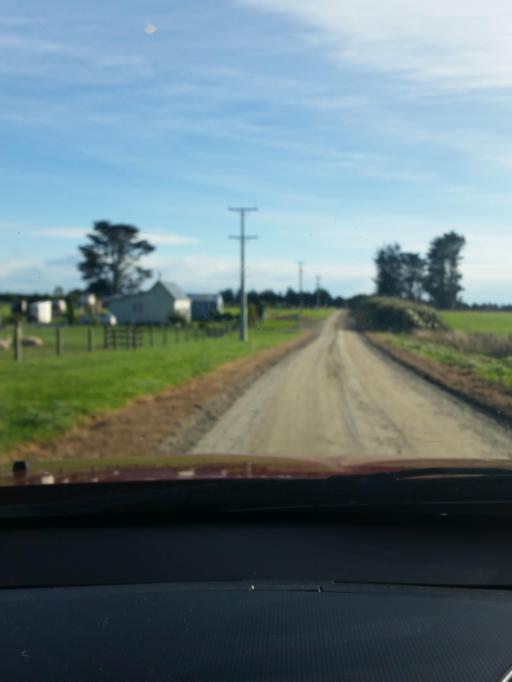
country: NZ
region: Southland
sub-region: Invercargill City
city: Invercargill
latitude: -46.3560
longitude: 168.5415
